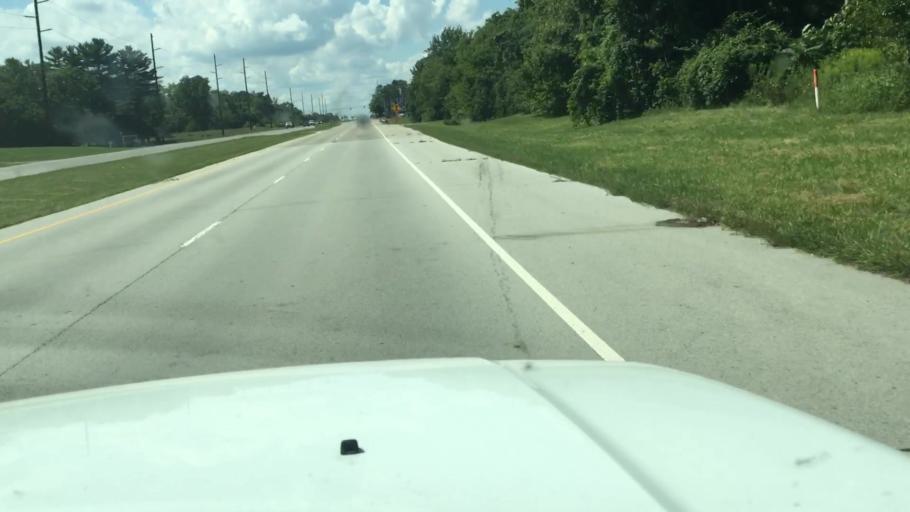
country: US
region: Ohio
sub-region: Clark County
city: Springfield
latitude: 39.9226
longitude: -83.7333
